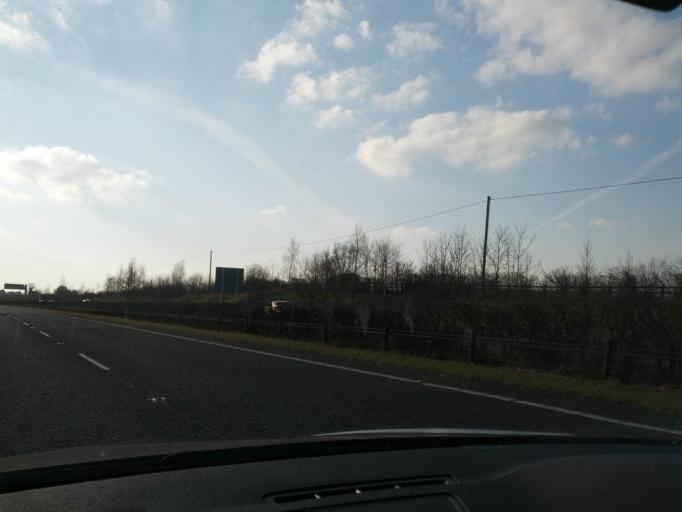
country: IE
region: Leinster
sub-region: Kildare
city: Cherryville
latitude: 53.1547
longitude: -6.9473
